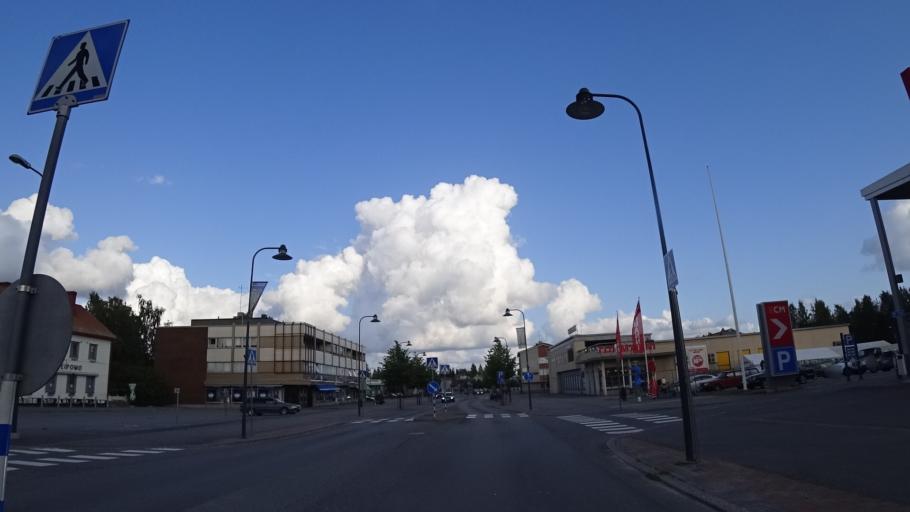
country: FI
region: North Karelia
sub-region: Pielisen Karjala
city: Lieksa
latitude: 63.3190
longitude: 30.0241
